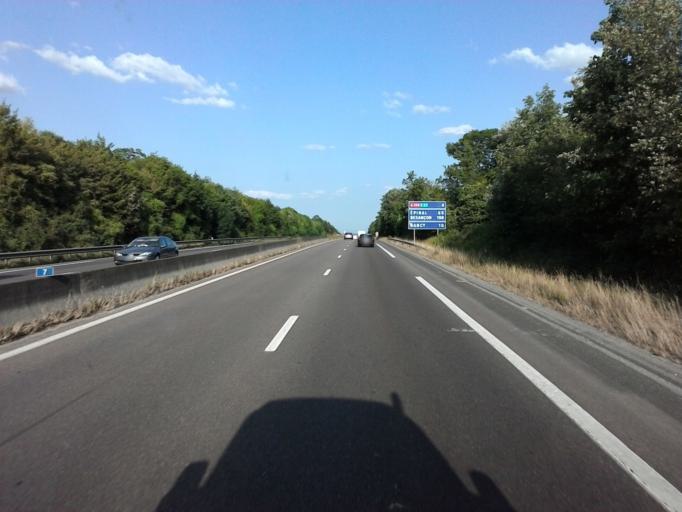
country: FR
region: Lorraine
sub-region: Departement de Meurthe-et-Moselle
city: Ludres
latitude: 48.6441
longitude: 6.1523
